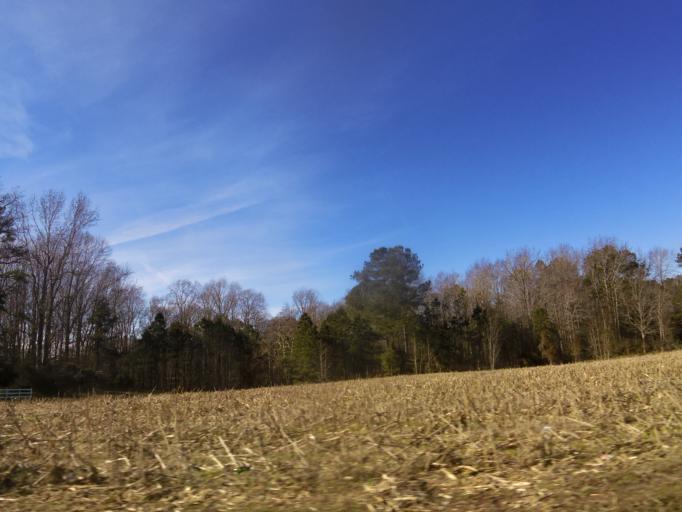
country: US
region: Virginia
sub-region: Isle of Wight County
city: Smithfield
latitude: 36.9639
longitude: -76.6624
